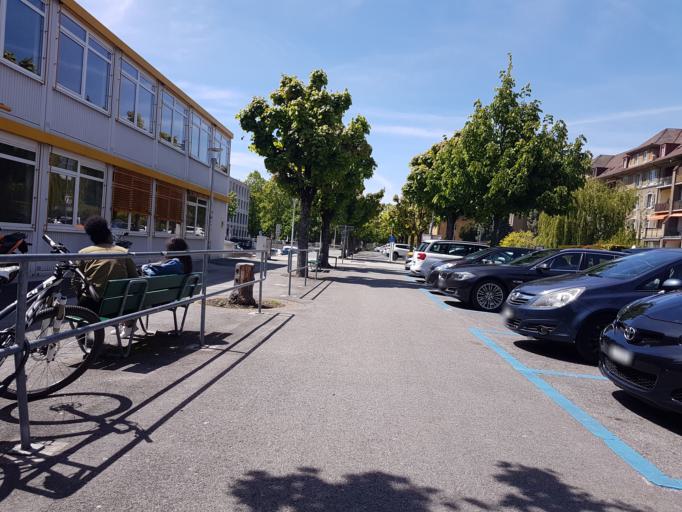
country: CH
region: Neuchatel
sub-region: Neuchatel District
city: Neuchatel
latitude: 46.9943
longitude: 6.9430
